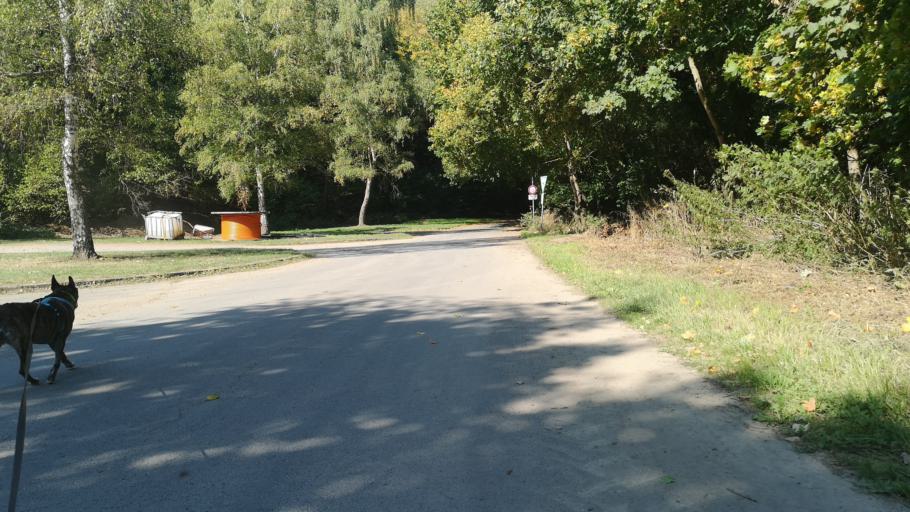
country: DE
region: North Rhine-Westphalia
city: Heimbach
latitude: 50.6381
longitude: 6.4659
